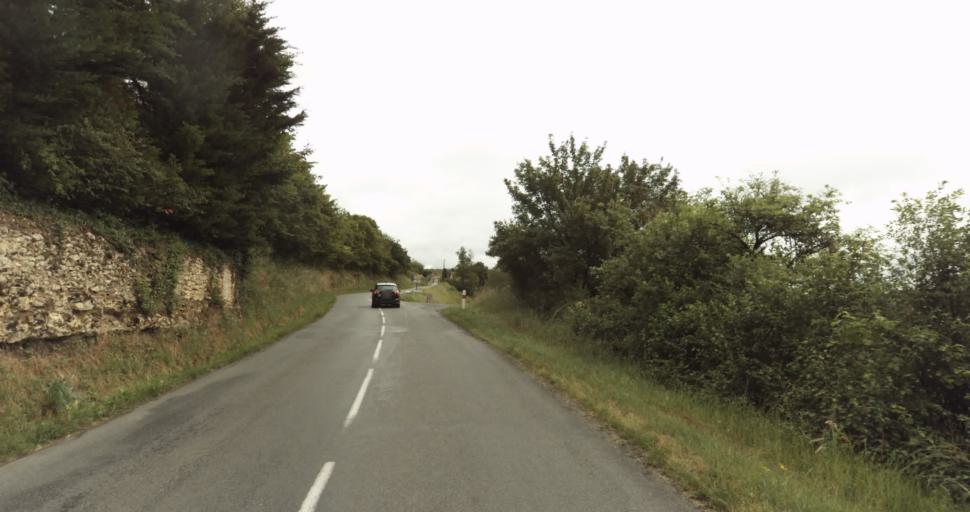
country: FR
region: Aquitaine
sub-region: Departement de la Dordogne
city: Belves
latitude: 44.6771
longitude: 0.8942
